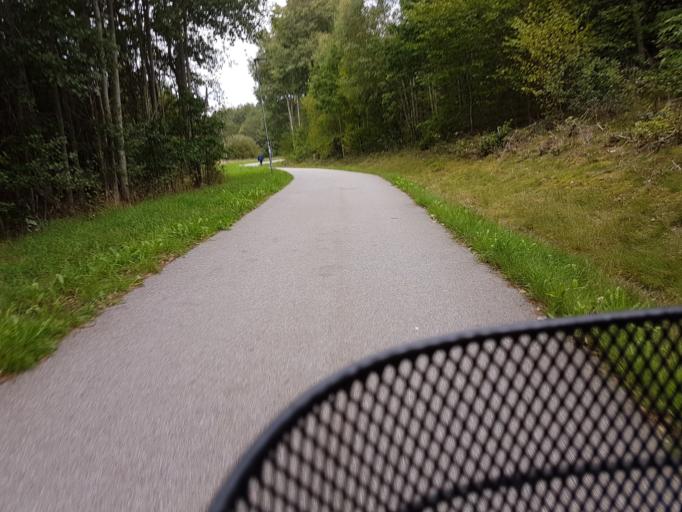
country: SE
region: Vaestra Goetaland
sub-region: Ale Kommun
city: Nodinge-Nol
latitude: 57.9011
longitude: 12.0589
